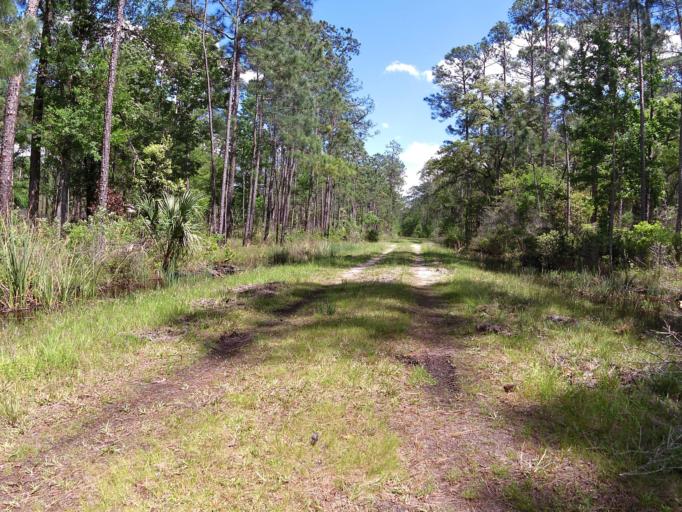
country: US
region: Florida
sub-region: Clay County
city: Green Cove Springs
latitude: 29.9661
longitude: -81.6397
